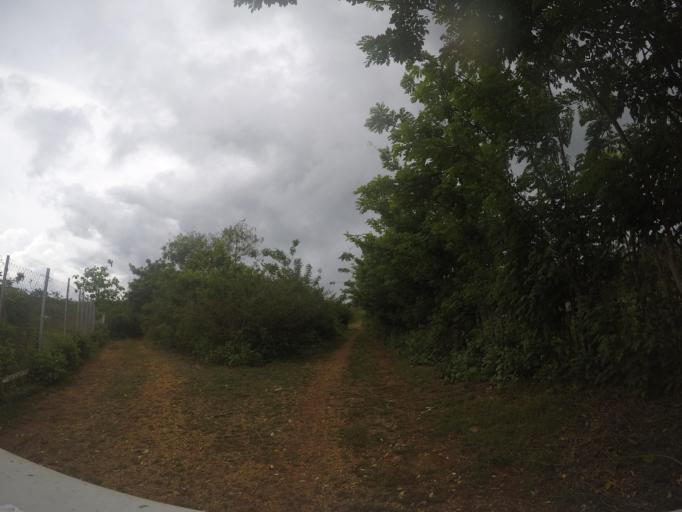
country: TL
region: Lautem
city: Lospalos
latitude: -8.5302
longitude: 126.9926
